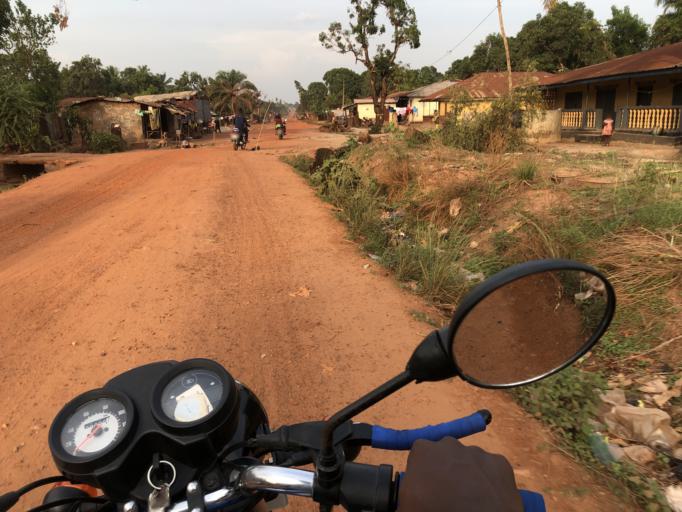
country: SL
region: Northern Province
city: Yonibana
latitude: 8.4666
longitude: -12.2115
